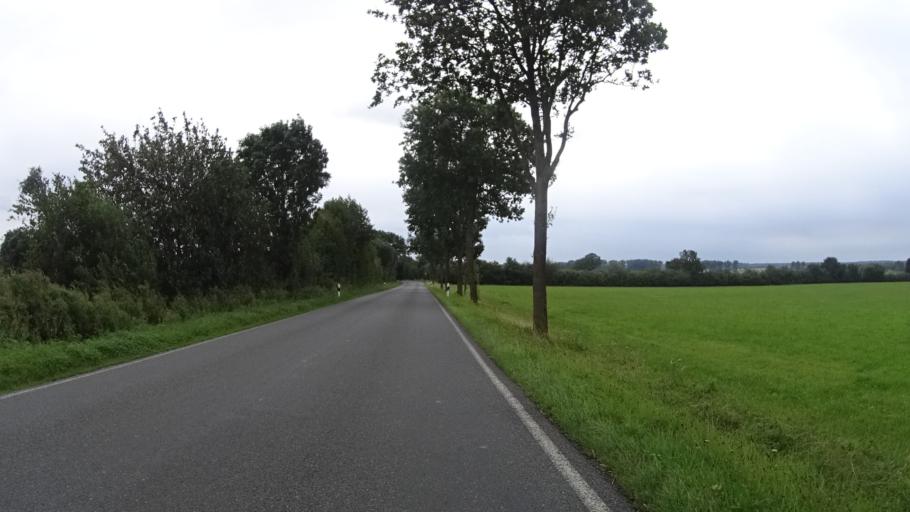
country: DE
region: Schleswig-Holstein
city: Duvensee
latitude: 53.7107
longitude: 10.5616
